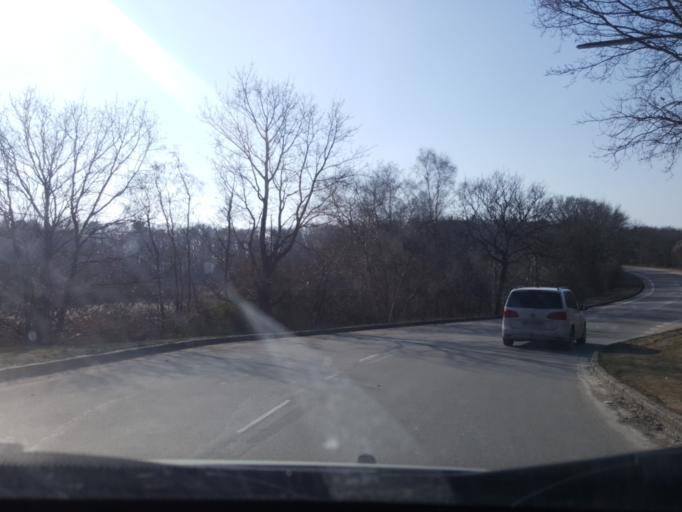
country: DK
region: Zealand
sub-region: Kalundborg Kommune
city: Kalundborg
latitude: 55.6866
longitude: 11.0740
